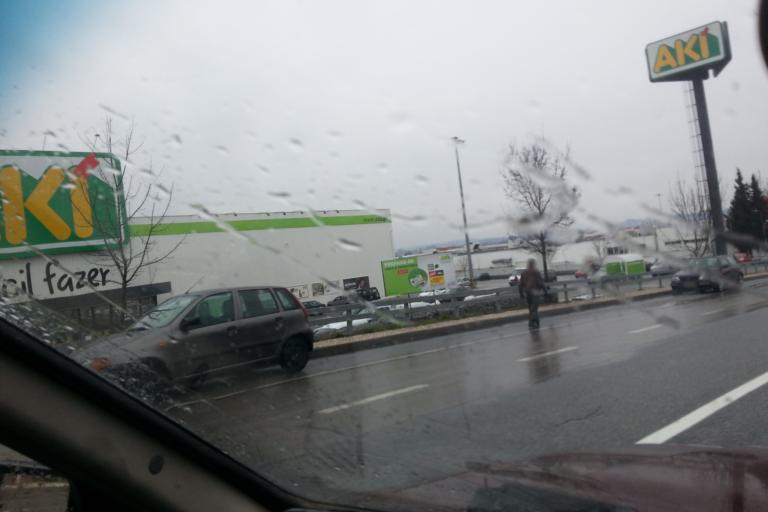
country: PT
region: Viseu
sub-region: Viseu
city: Abraveses
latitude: 40.6727
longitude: -7.9216
